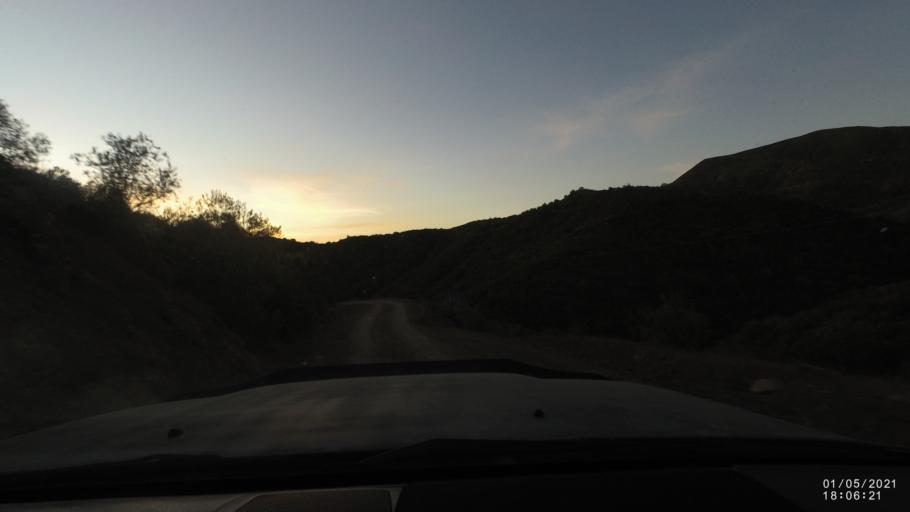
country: BO
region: Cochabamba
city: Capinota
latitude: -17.6873
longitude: -66.1847
